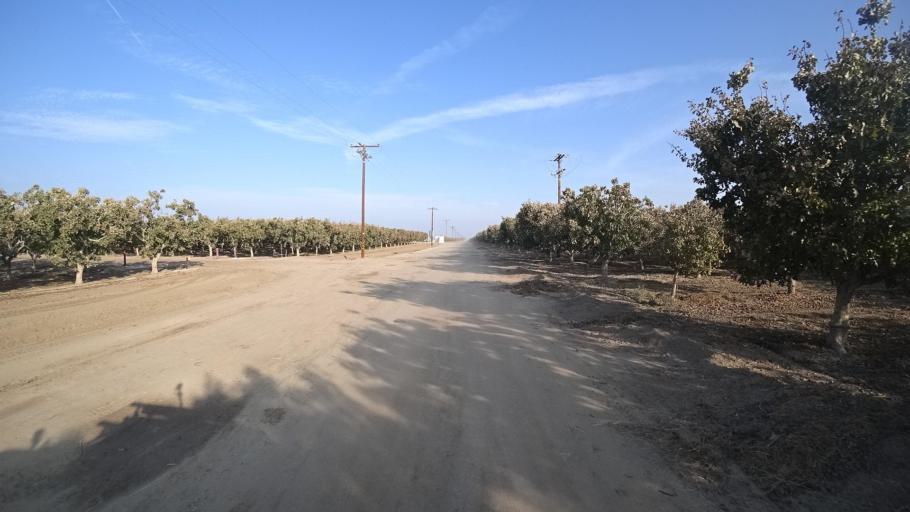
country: US
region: California
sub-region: Kern County
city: McFarland
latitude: 35.7249
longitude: -119.1872
